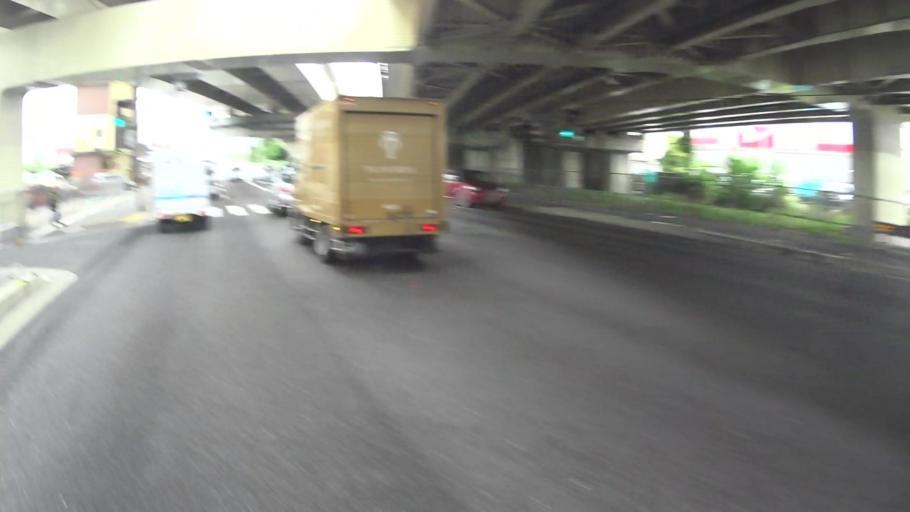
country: JP
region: Kyoto
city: Yawata
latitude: 34.9062
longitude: 135.6990
